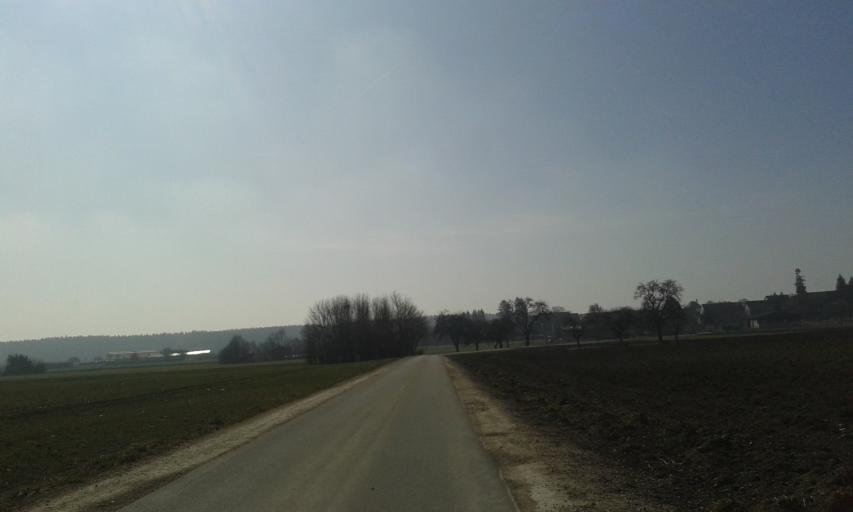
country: DE
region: Baden-Wuerttemberg
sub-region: Tuebingen Region
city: Griesingen
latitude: 48.2728
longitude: 9.7876
